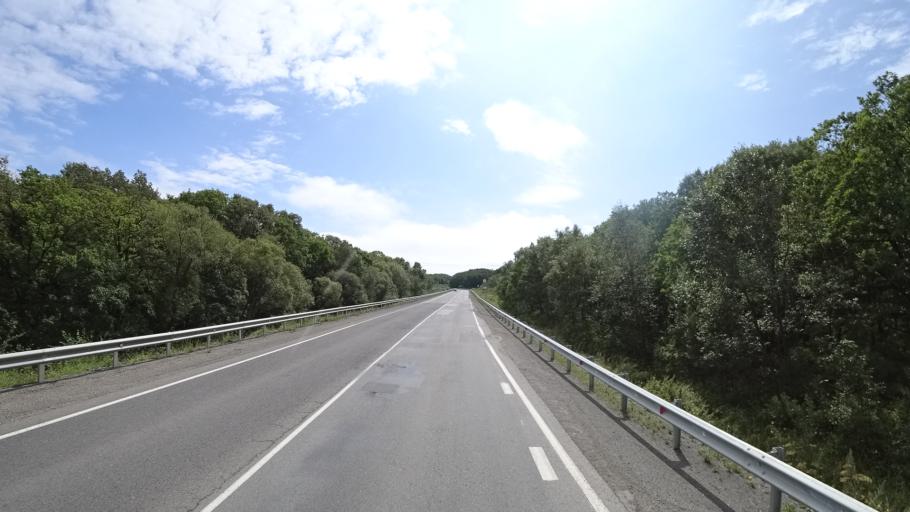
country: RU
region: Primorskiy
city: Lyalichi
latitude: 44.1364
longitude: 132.4281
